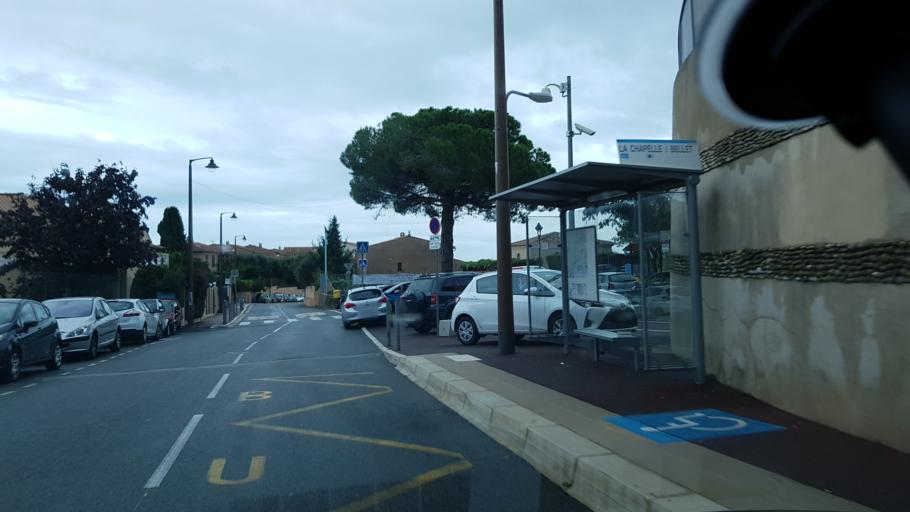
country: FR
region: Provence-Alpes-Cote d'Azur
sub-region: Departement des Alpes-Maritimes
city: Nice
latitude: 43.7035
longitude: 7.2275
